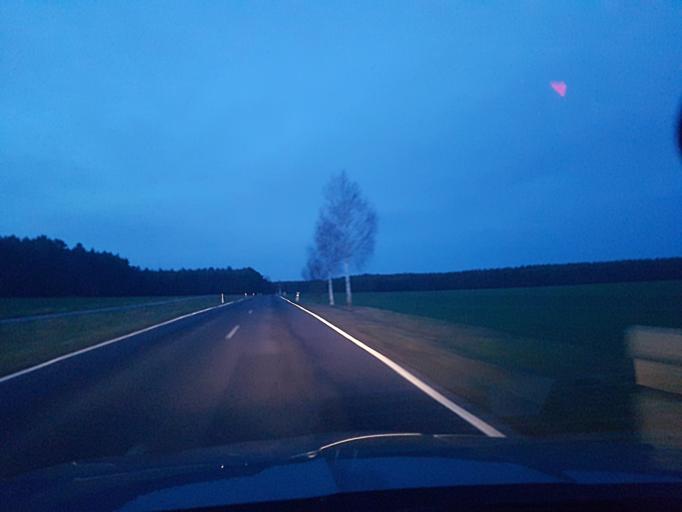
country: DE
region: Brandenburg
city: Trobitz
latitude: 51.5632
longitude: 13.4196
